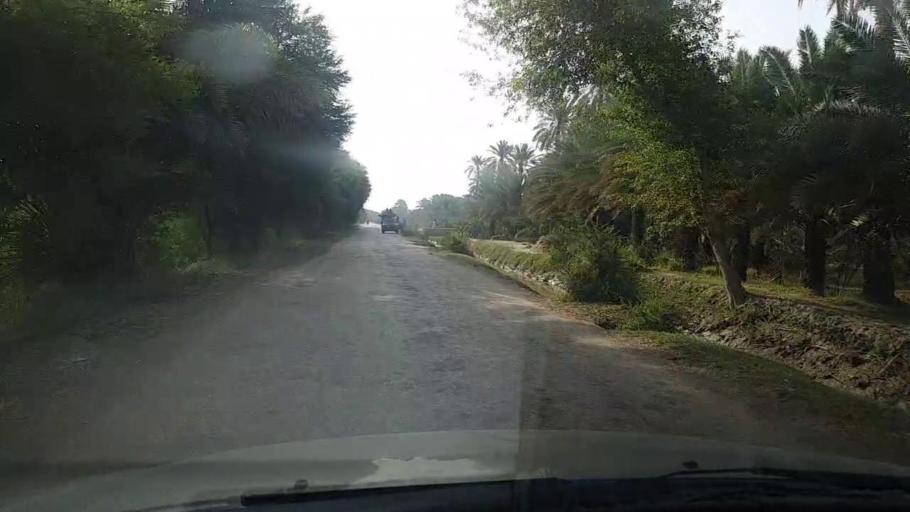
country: PK
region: Sindh
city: Pir jo Goth
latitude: 27.5622
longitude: 68.5415
